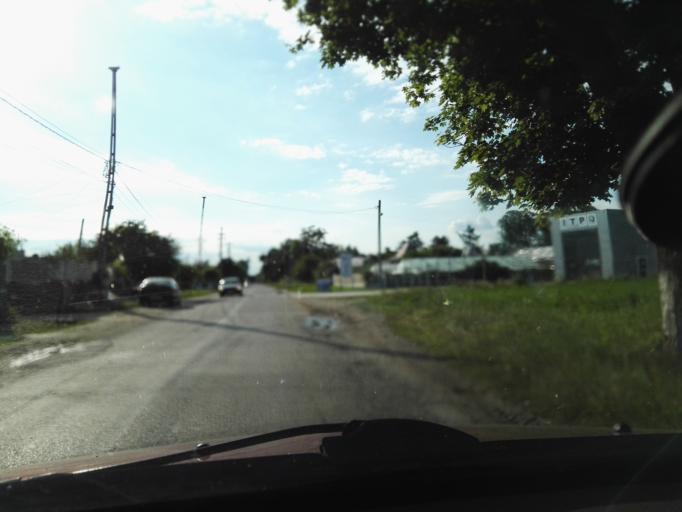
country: RO
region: Ilfov
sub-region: Comuna Copaceni
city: Copaceni
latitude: 44.2417
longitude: 26.1043
